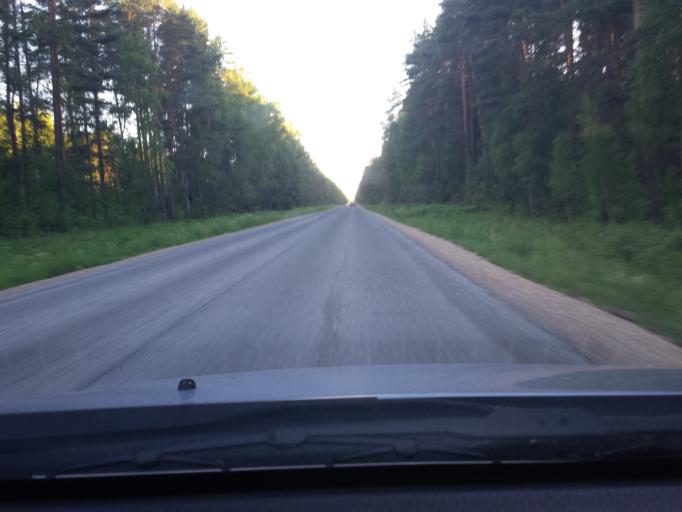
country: LV
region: Carnikava
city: Carnikava
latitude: 57.1109
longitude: 24.2325
